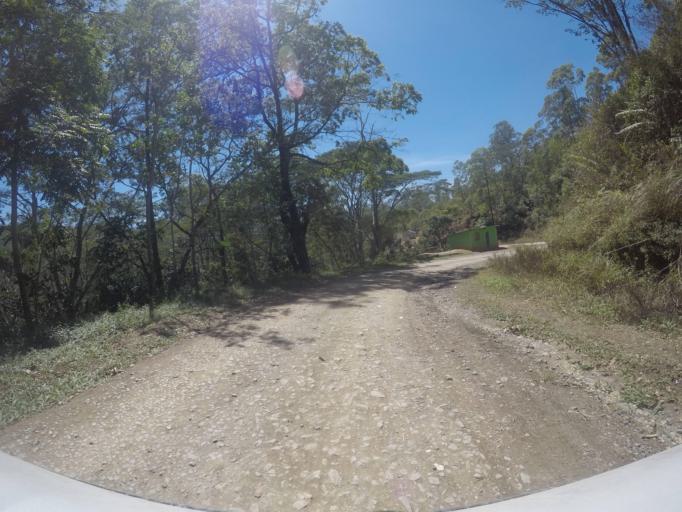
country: TL
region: Ermera
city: Gleno
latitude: -8.7823
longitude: 125.3766
